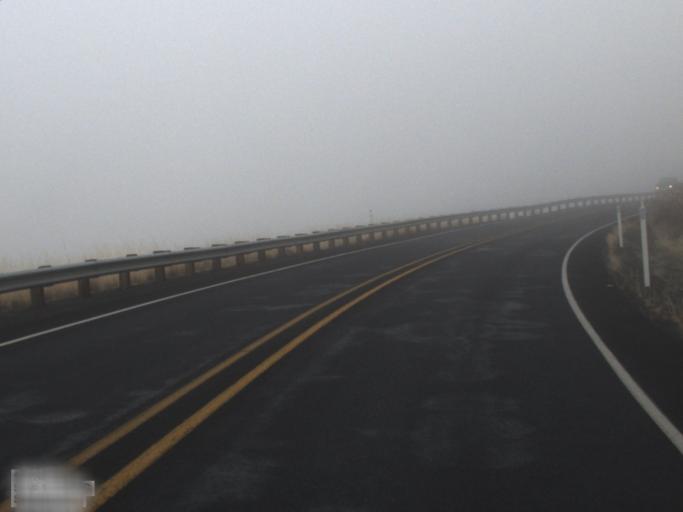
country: US
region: Washington
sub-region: Asotin County
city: Asotin
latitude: 46.3194
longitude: -117.0491
